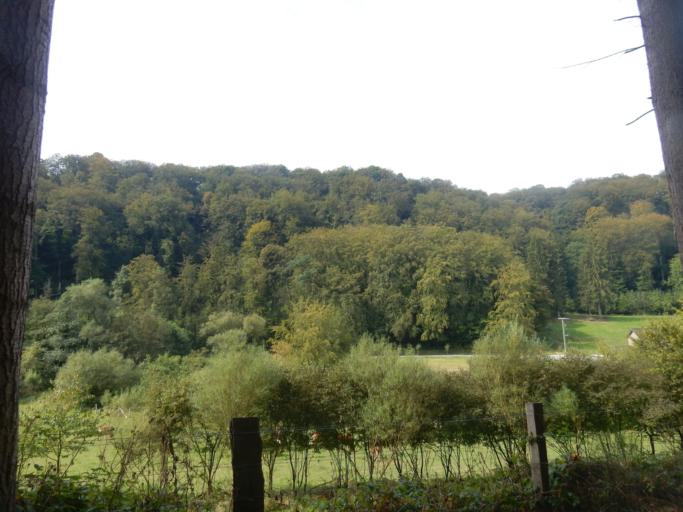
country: LU
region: Luxembourg
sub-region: Canton de Mersch
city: Mersch
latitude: 49.7277
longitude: 6.0814
